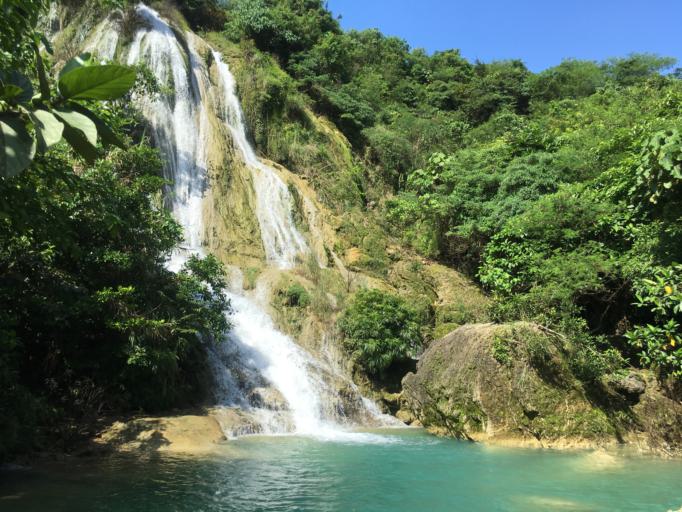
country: PH
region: Ilocos
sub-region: Province of Pangasinan
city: Ranao
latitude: 16.2216
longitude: 119.8331
